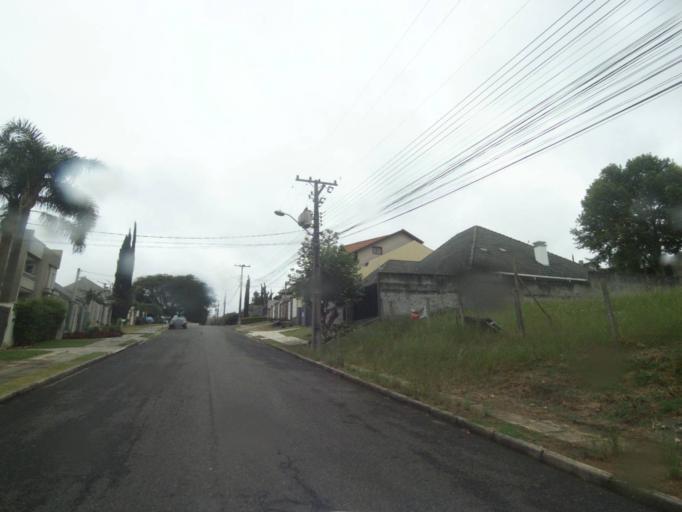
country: BR
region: Parana
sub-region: Curitiba
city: Curitiba
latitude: -25.4251
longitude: -49.3229
